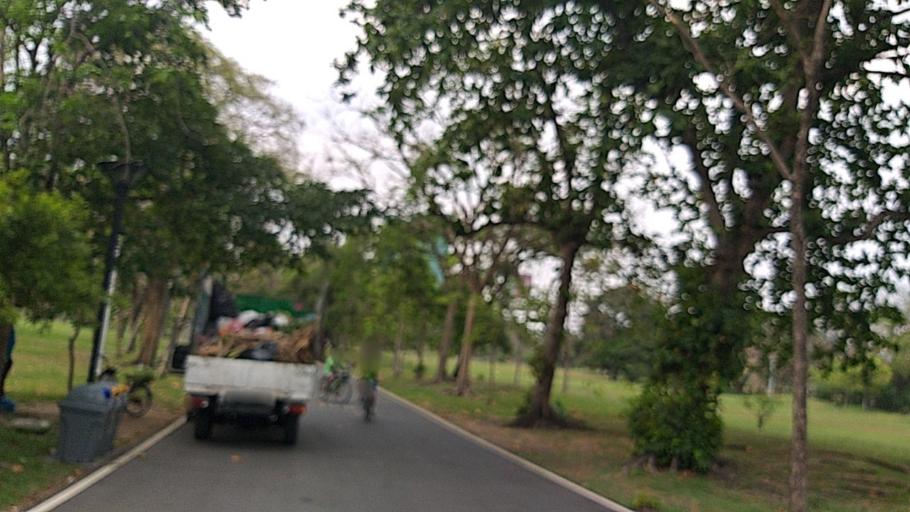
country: TH
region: Bangkok
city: Chatuchak
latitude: 13.8125
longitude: 100.5550
